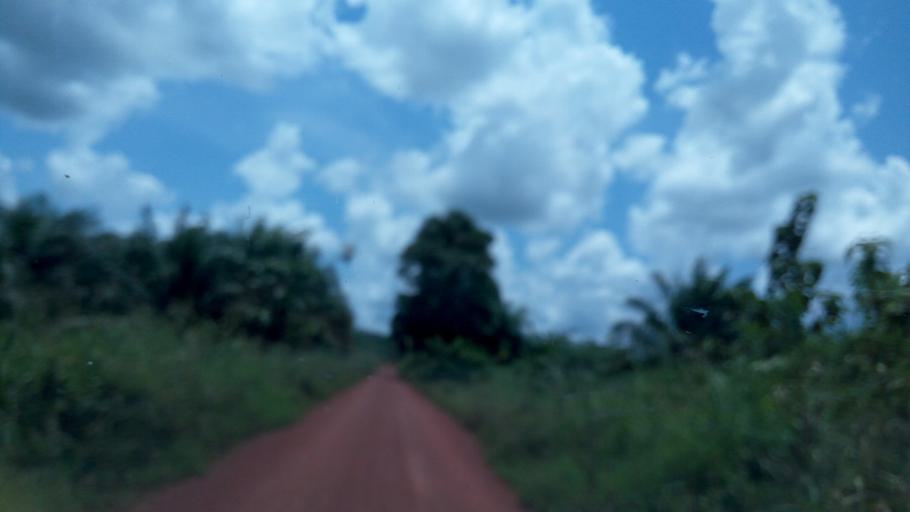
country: CD
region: Equateur
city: Libenge
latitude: 3.7524
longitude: 19.0595
